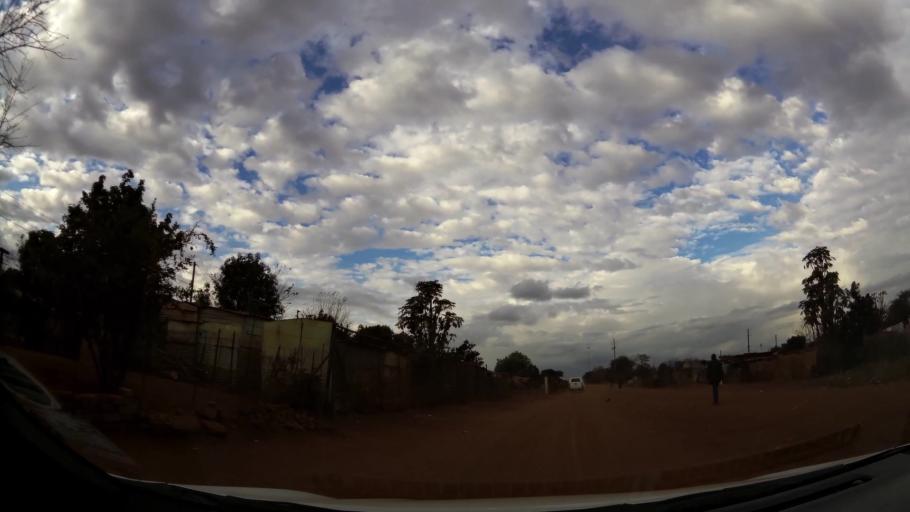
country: ZA
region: Limpopo
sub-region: Waterberg District Municipality
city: Modimolle
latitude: -24.5263
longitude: 28.7218
